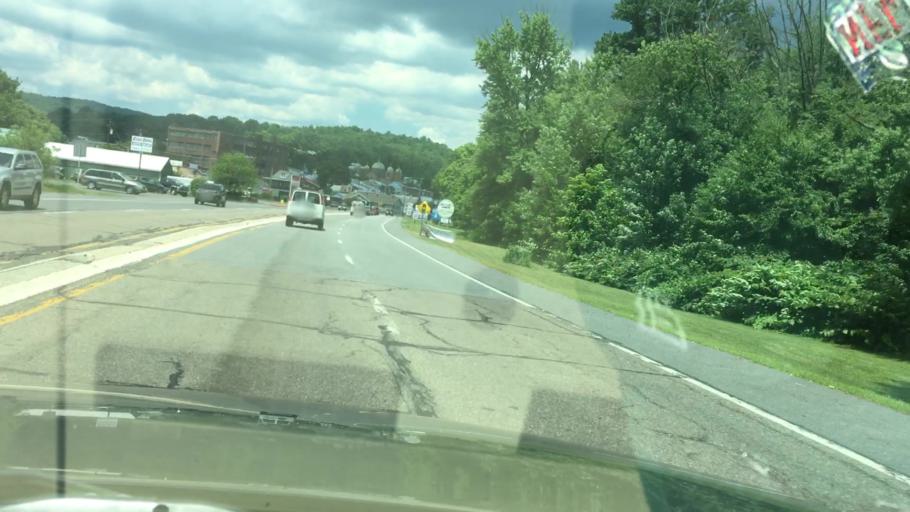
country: US
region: Pennsylvania
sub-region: Schuylkill County
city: Minersville
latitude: 40.6879
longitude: -76.2561
